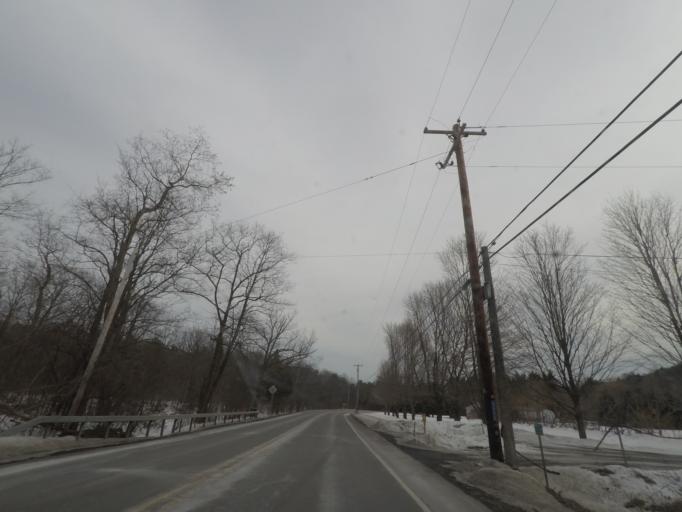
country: US
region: New York
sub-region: Albany County
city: Voorheesville
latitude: 42.5905
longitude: -73.9843
